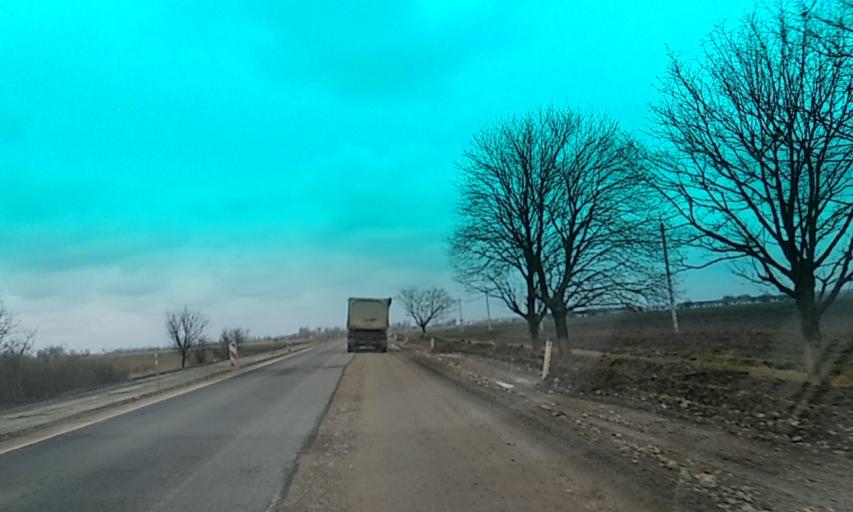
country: RU
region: Krasnodarskiy
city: Velikovechnoye
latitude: 44.9927
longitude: 39.7135
